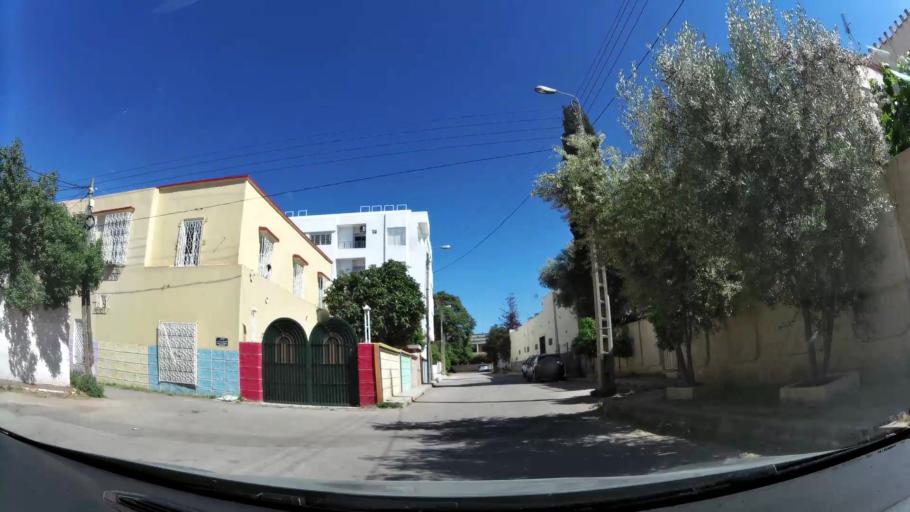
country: MA
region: Fes-Boulemane
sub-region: Fes
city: Fes
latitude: 34.0234
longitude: -4.9918
